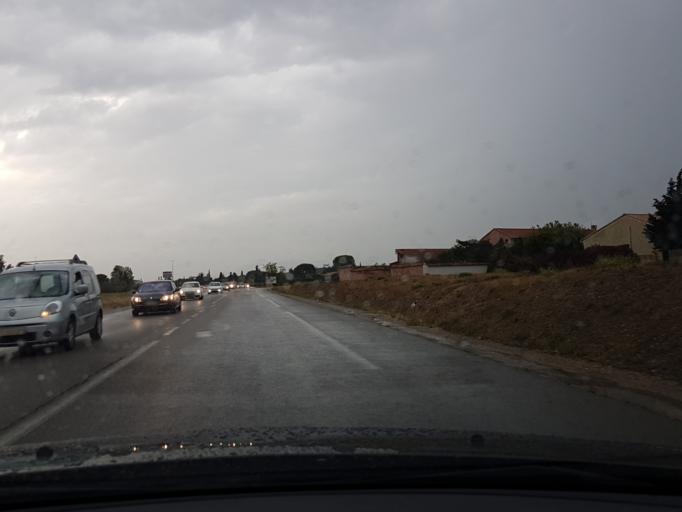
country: FR
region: Provence-Alpes-Cote d'Azur
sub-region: Departement du Vaucluse
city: Carpentras
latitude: 44.0417
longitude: 5.0304
